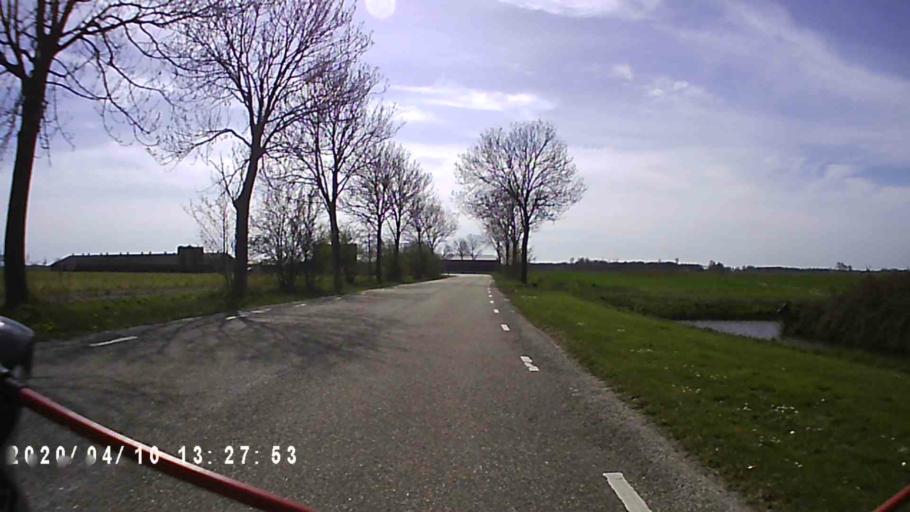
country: NL
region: Groningen
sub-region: Gemeente Zuidhorn
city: Oldehove
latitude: 53.3786
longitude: 6.4212
